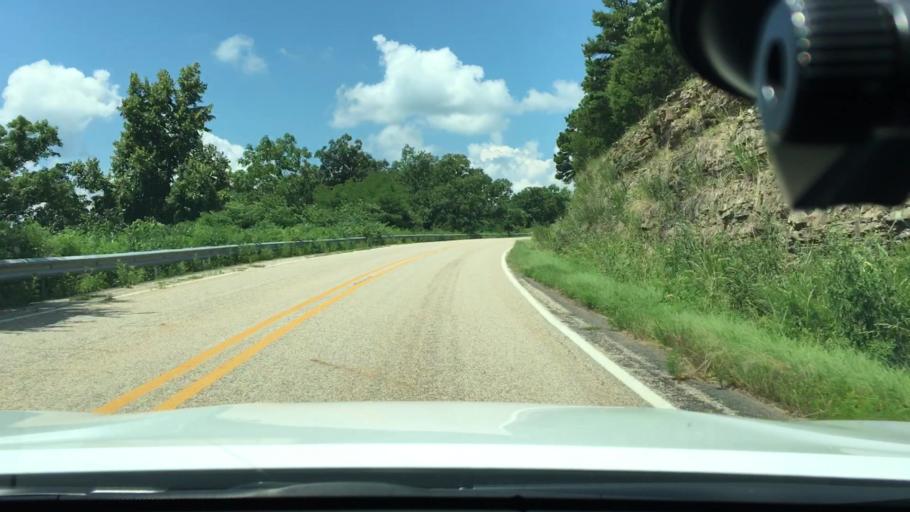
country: US
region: Arkansas
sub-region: Logan County
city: Paris
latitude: 35.1758
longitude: -93.5895
